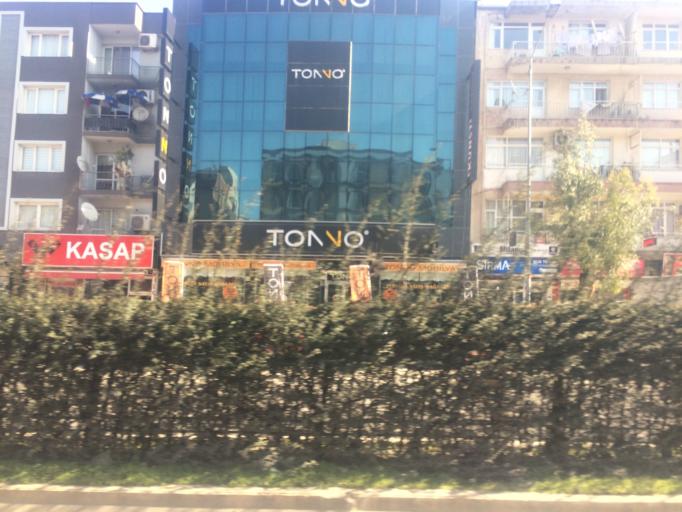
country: TR
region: Izmir
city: Karsiyaka
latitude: 38.4997
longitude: 27.0557
